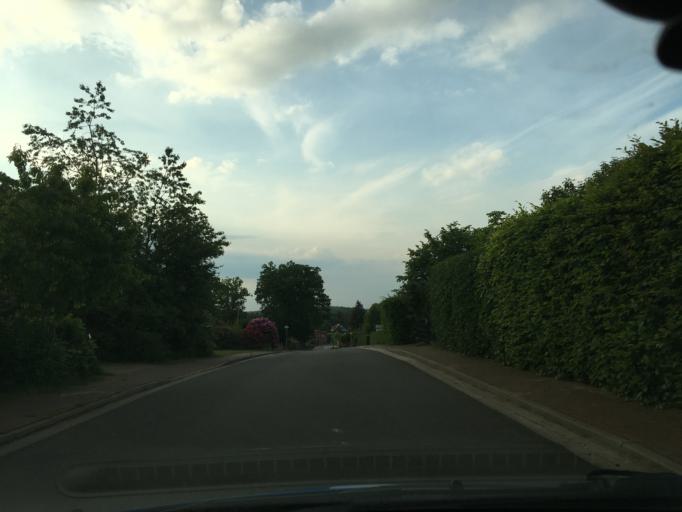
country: DE
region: Lower Saxony
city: Amelinghausen
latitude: 53.1303
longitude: 10.2106
